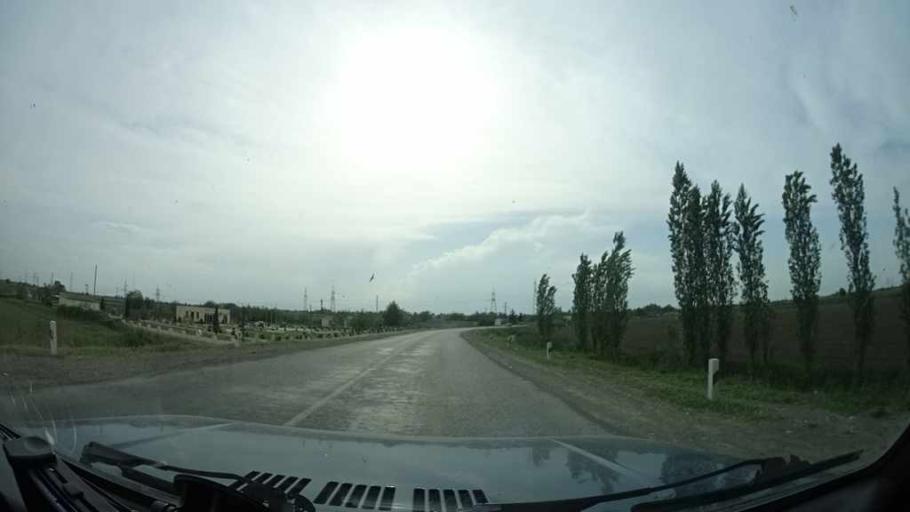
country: AZ
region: Barda Rayon
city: Barda
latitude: 40.3393
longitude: 47.1811
